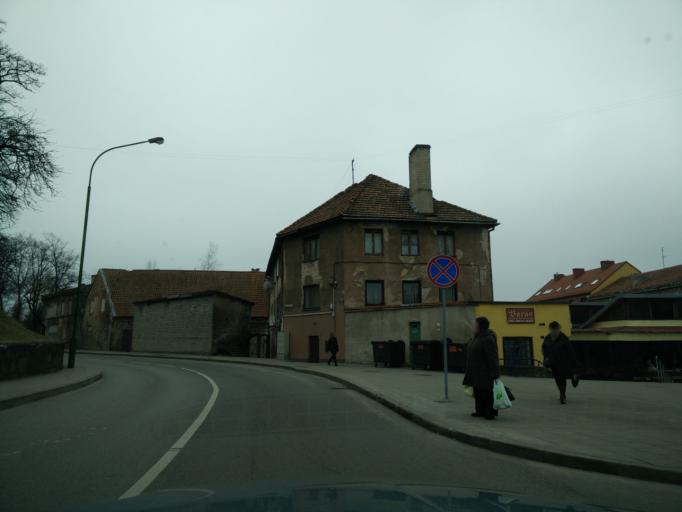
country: LT
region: Klaipedos apskritis
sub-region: Klaipeda
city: Klaipeda
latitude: 55.7065
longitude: 21.1386
